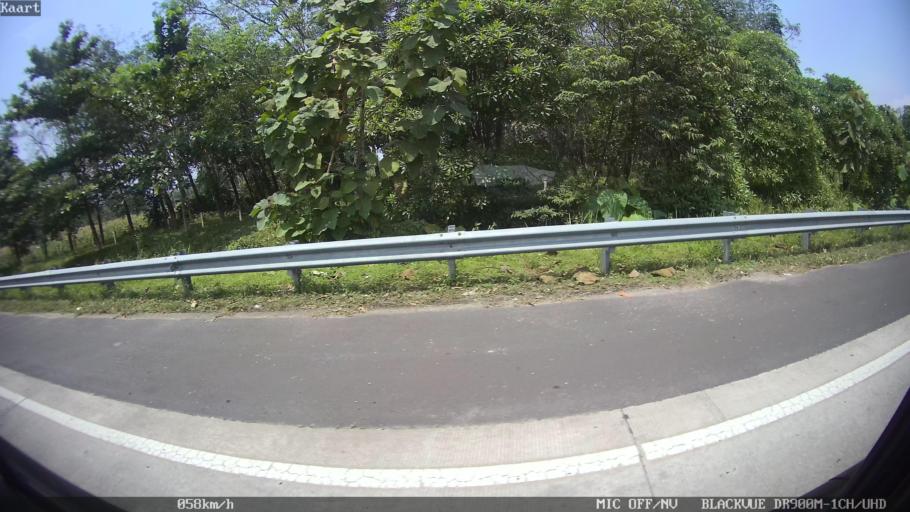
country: ID
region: Lampung
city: Kedaton
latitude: -5.3790
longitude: 105.3312
